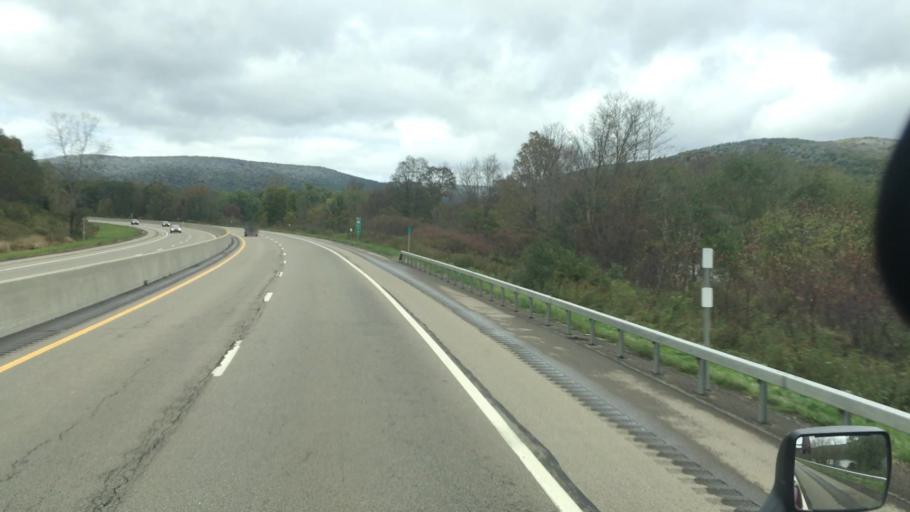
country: US
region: New York
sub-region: Cattaraugus County
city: Salamanca
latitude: 42.1443
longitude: -78.6685
